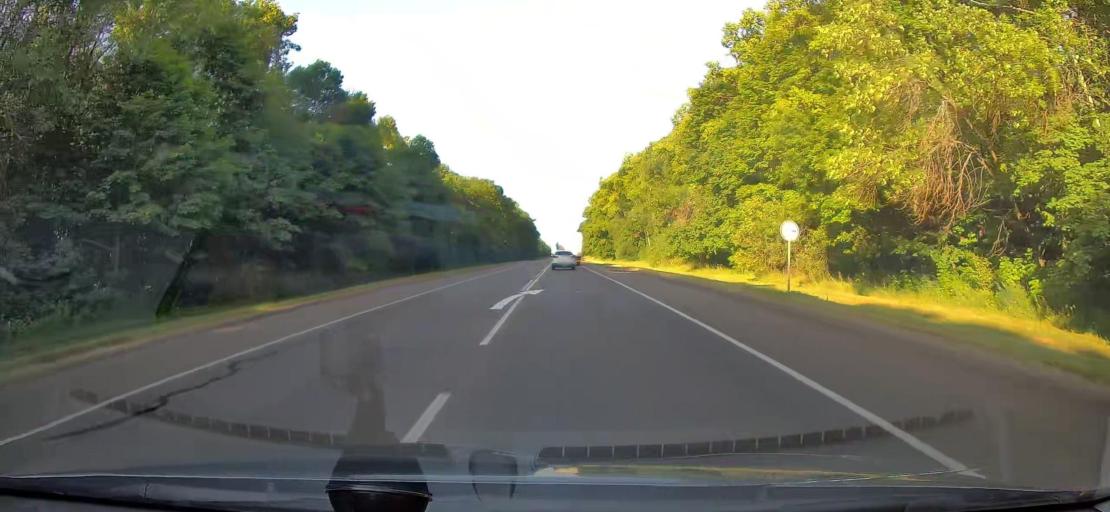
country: RU
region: Tula
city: Chern'
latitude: 53.4802
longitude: 36.9879
